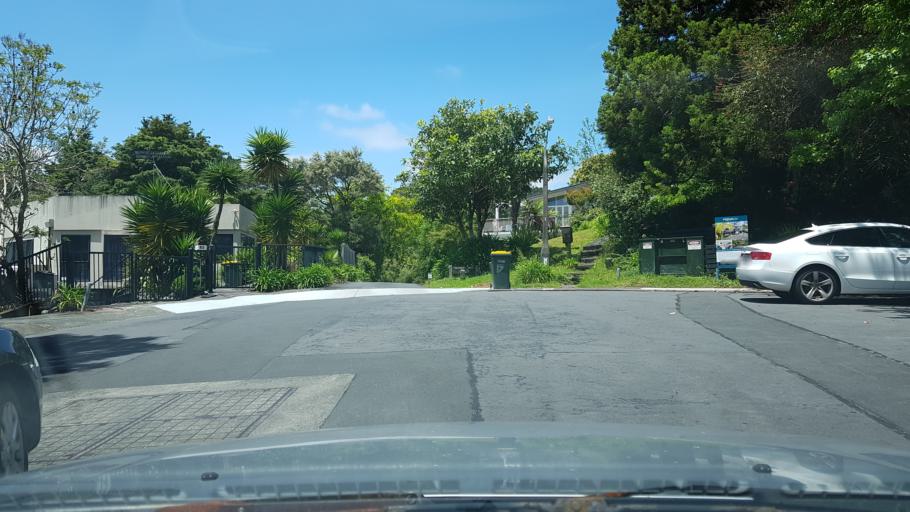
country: NZ
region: Auckland
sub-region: Auckland
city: North Shore
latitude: -36.8036
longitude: 174.7170
